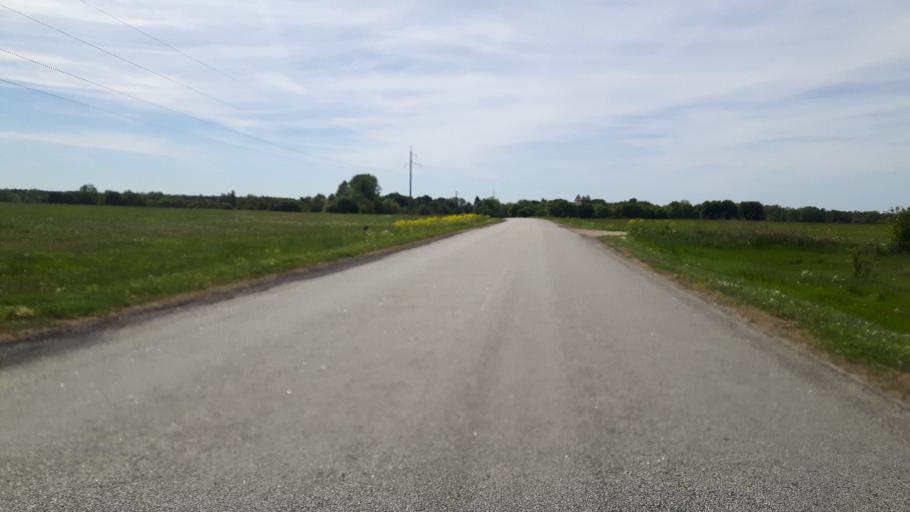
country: EE
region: Harju
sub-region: Raasiku vald
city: Raasiku
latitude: 59.4685
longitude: 25.2649
